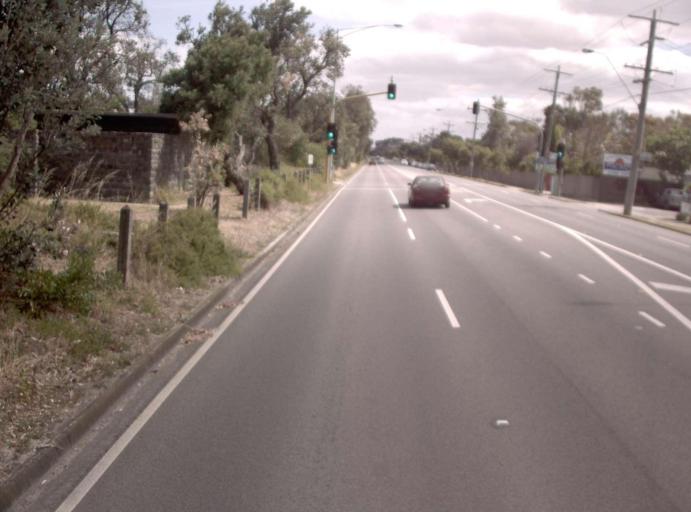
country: AU
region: Victoria
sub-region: Frankston
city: Frankston East
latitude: -38.1216
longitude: 145.1247
